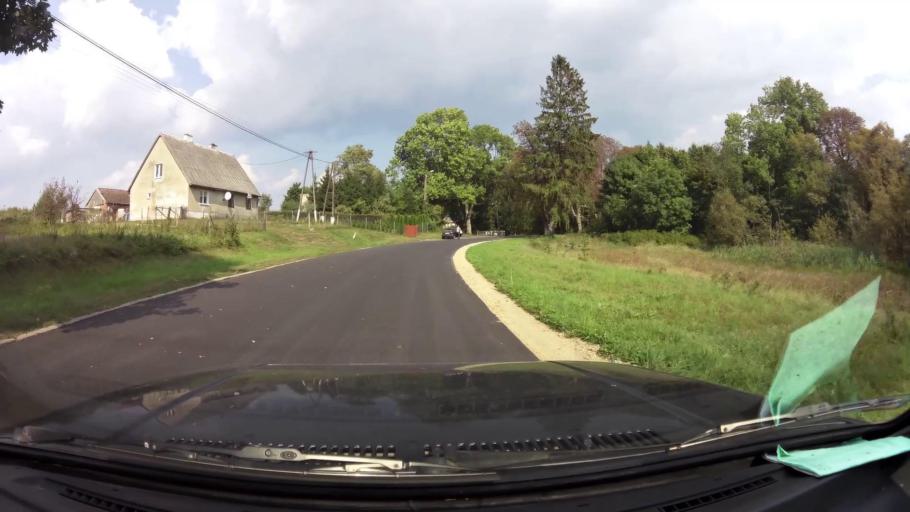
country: PL
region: Pomeranian Voivodeship
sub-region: Powiat slupski
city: Kepice
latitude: 54.1682
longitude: 16.8209
